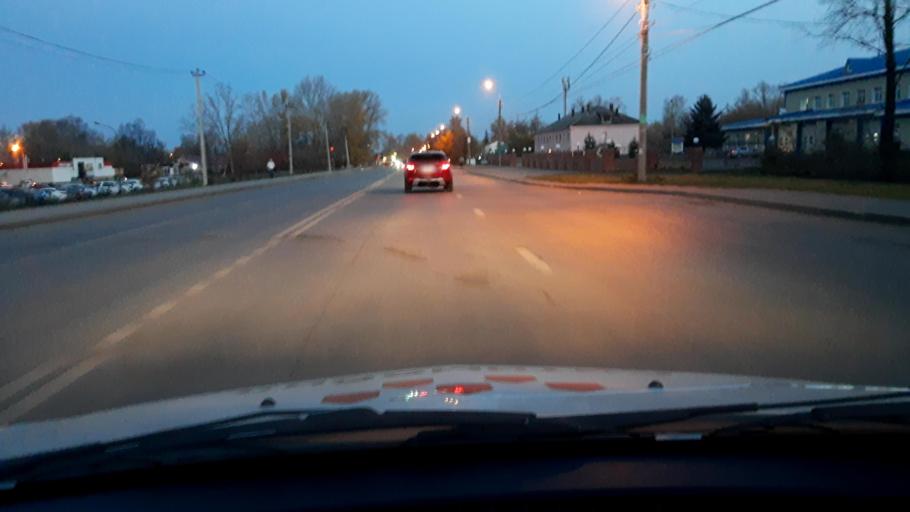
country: RU
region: Bashkortostan
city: Iglino
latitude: 54.7697
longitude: 56.2316
